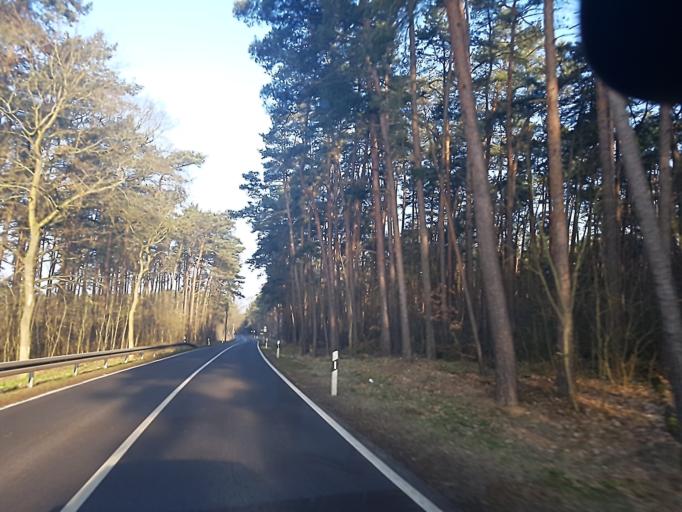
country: DE
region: Brandenburg
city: Golzow
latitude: 52.2719
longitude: 12.6367
